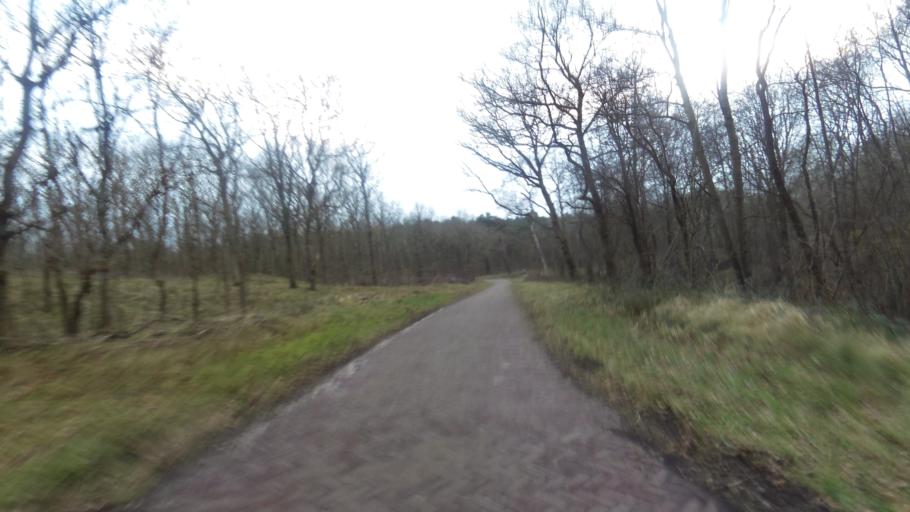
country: NL
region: North Holland
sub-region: Gemeente Bergen
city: Egmond aan Zee
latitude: 52.6670
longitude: 4.6498
